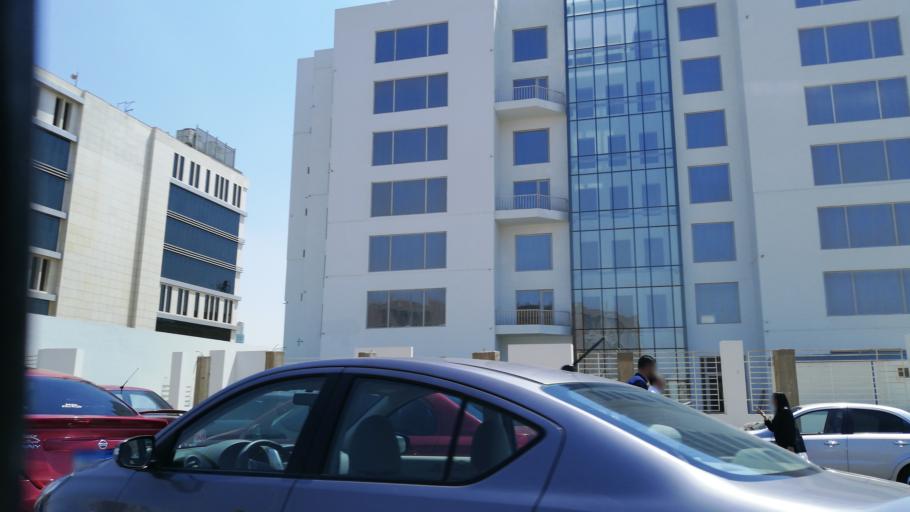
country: EG
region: Muhafazat al Qahirah
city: Cairo
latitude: 30.0195
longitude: 31.4263
